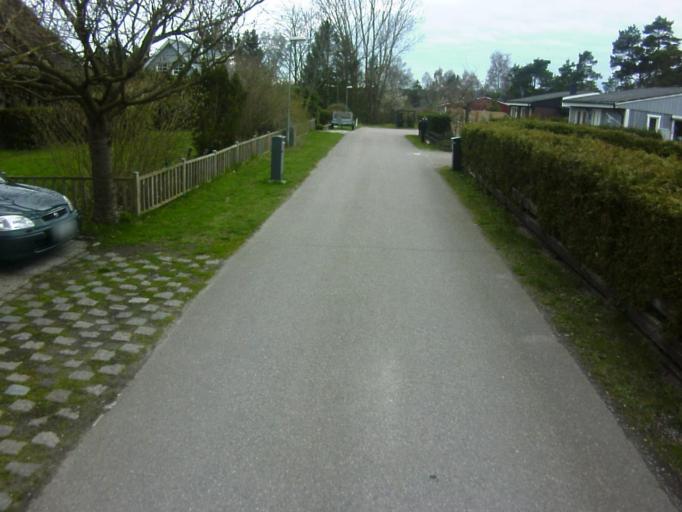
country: SE
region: Skane
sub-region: Kavlinge Kommun
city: Hofterup
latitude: 55.7946
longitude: 12.9727
